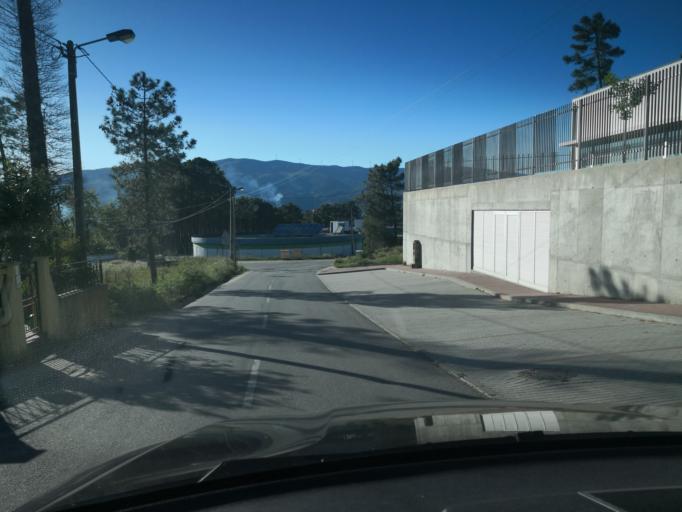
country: PT
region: Vila Real
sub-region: Vila Real
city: Vila Real
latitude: 41.3151
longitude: -7.6962
